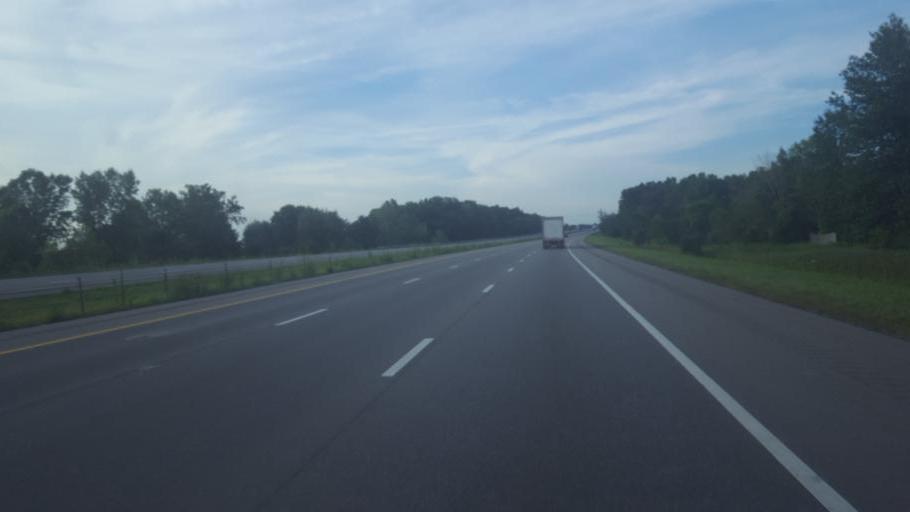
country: US
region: Ohio
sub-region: Morrow County
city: Cardington
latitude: 40.4226
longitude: -82.8196
